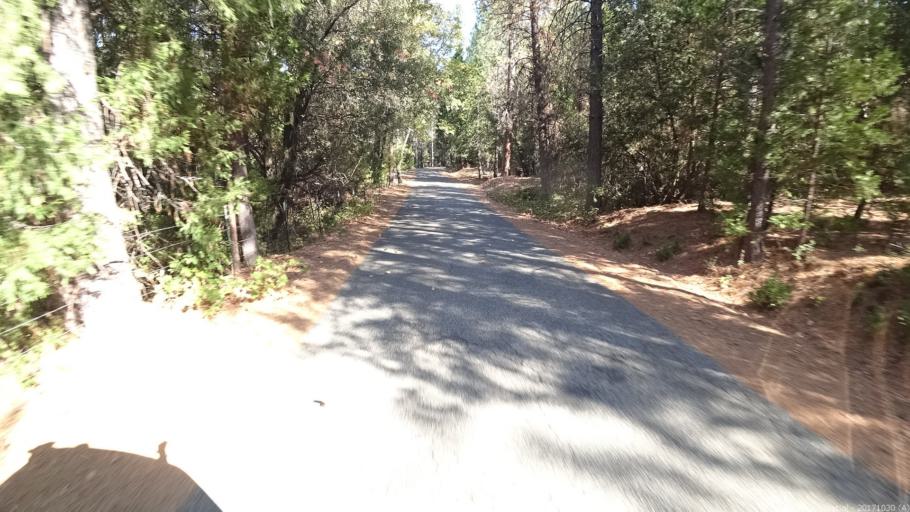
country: US
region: California
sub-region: Shasta County
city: Shingletown
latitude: 40.5665
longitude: -121.8867
